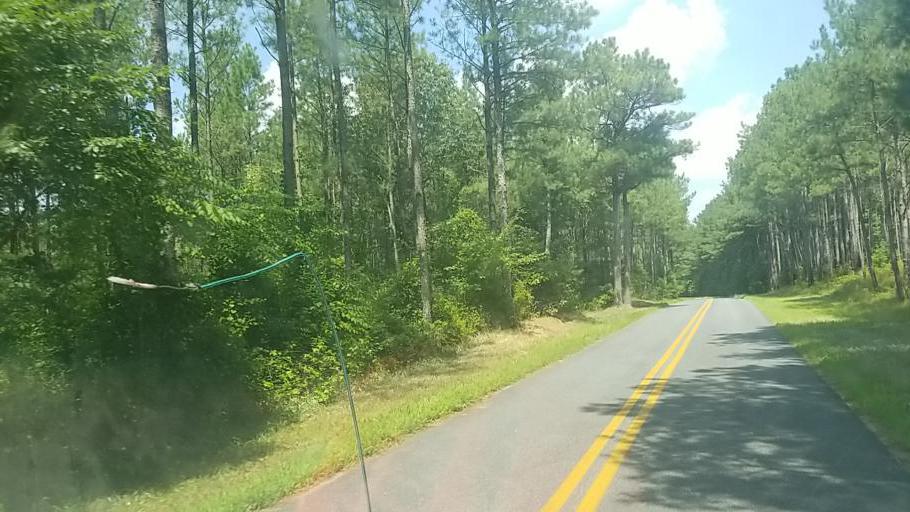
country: US
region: Maryland
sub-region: Worcester County
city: Snow Hill
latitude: 38.2750
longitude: -75.4730
